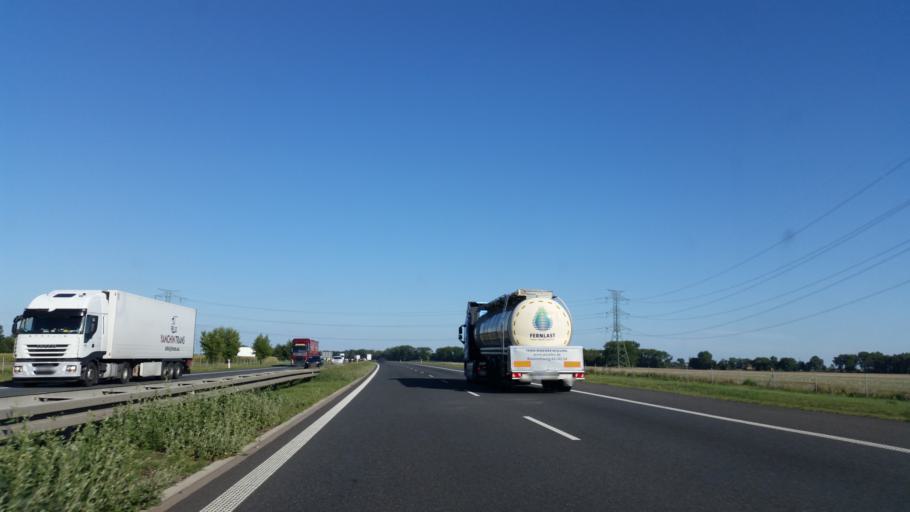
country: PL
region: Opole Voivodeship
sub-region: Powiat brzeski
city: Grodkow
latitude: 50.7735
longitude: 17.3683
